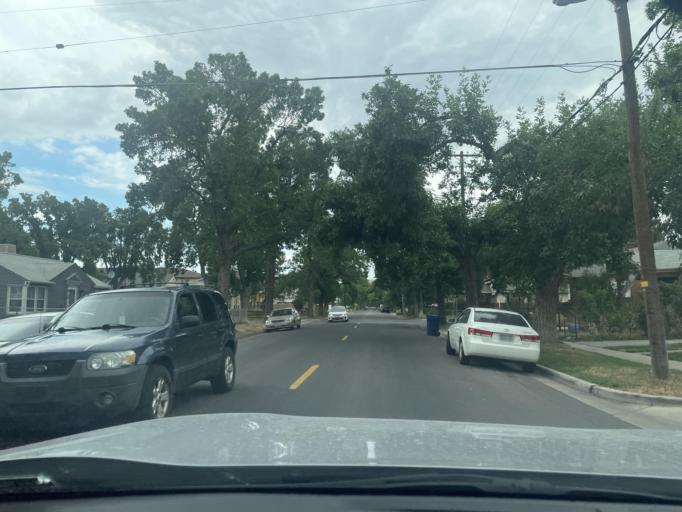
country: US
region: Utah
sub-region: Salt Lake County
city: South Salt Lake
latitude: 40.7293
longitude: -111.8940
